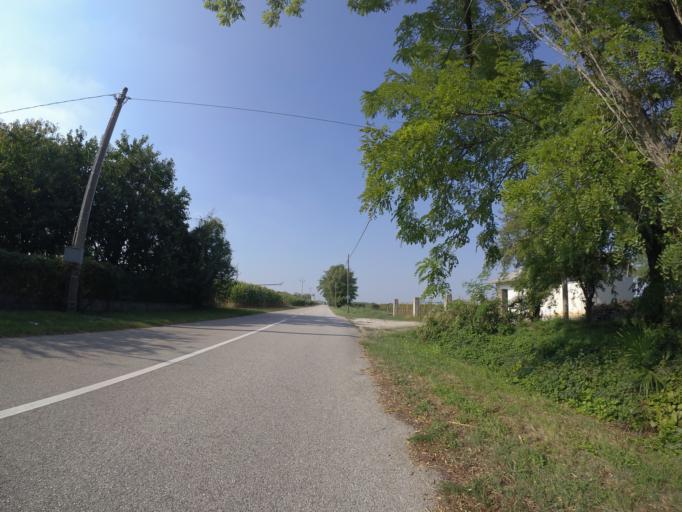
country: IT
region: Friuli Venezia Giulia
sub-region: Provincia di Udine
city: Bertiolo
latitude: 45.9792
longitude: 13.0368
